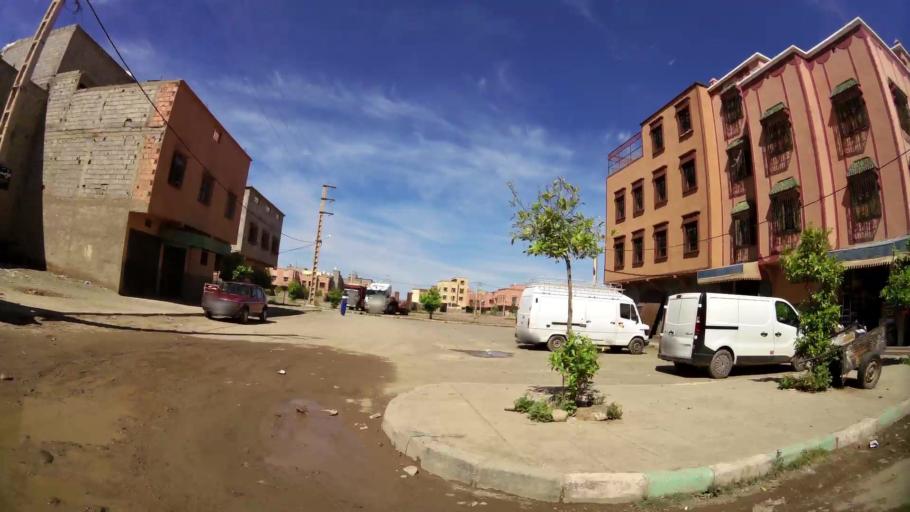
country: MA
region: Marrakech-Tensift-Al Haouz
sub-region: Marrakech
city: Marrakesh
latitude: 31.6423
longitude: -8.1139
